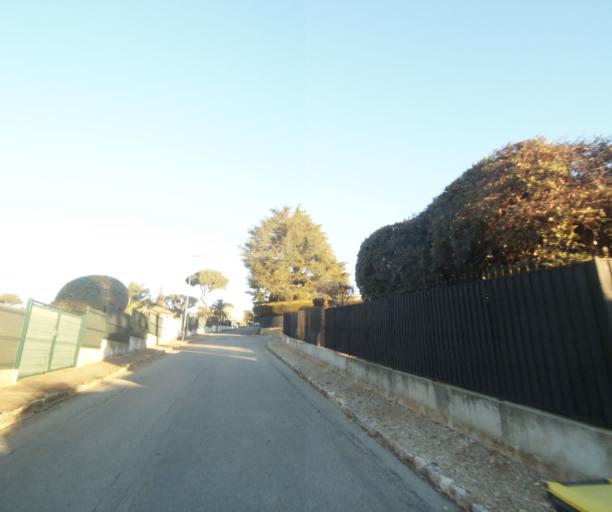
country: FR
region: Provence-Alpes-Cote d'Azur
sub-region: Departement des Alpes-Maritimes
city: Vallauris
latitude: 43.5808
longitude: 7.0828
